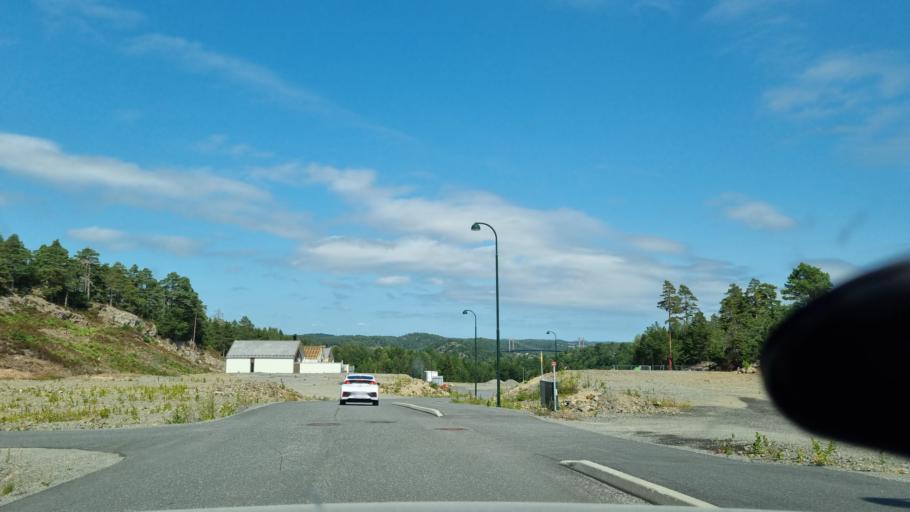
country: NO
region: Aust-Agder
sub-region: Arendal
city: Arendal
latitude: 58.4584
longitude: 8.8135
